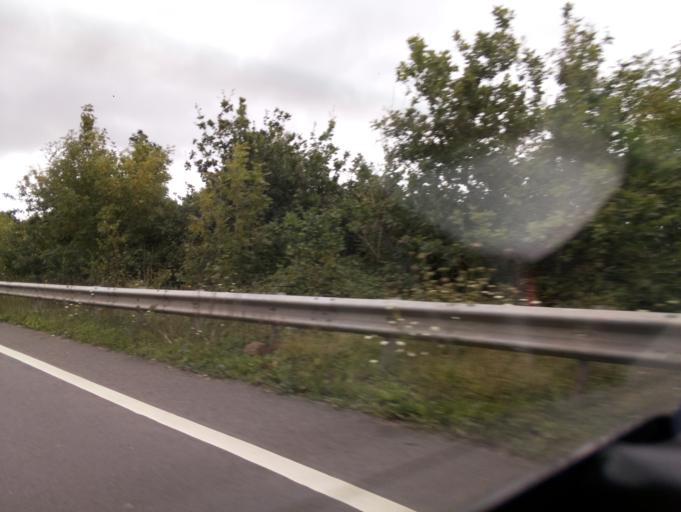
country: GB
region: England
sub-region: Devon
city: Marldon
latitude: 50.4557
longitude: -3.5904
